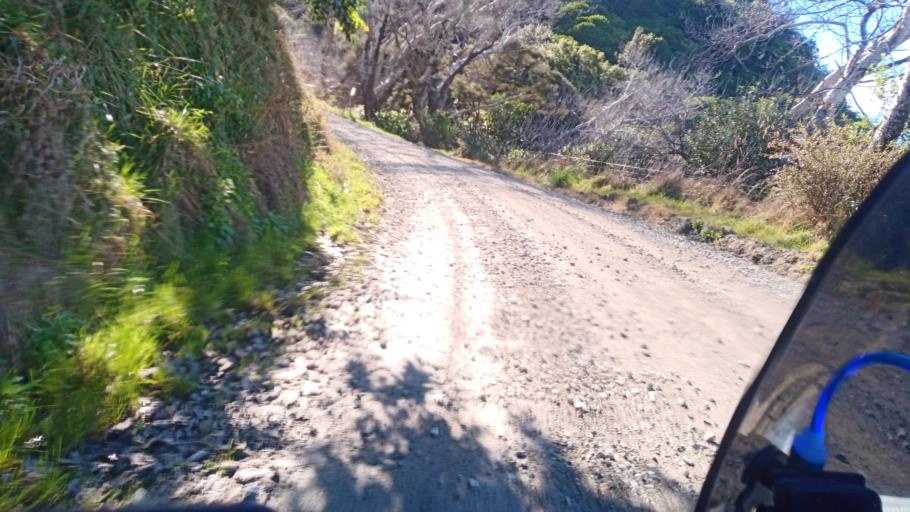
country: NZ
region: Gisborne
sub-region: Gisborne District
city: Gisborne
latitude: -38.2280
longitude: 178.3107
